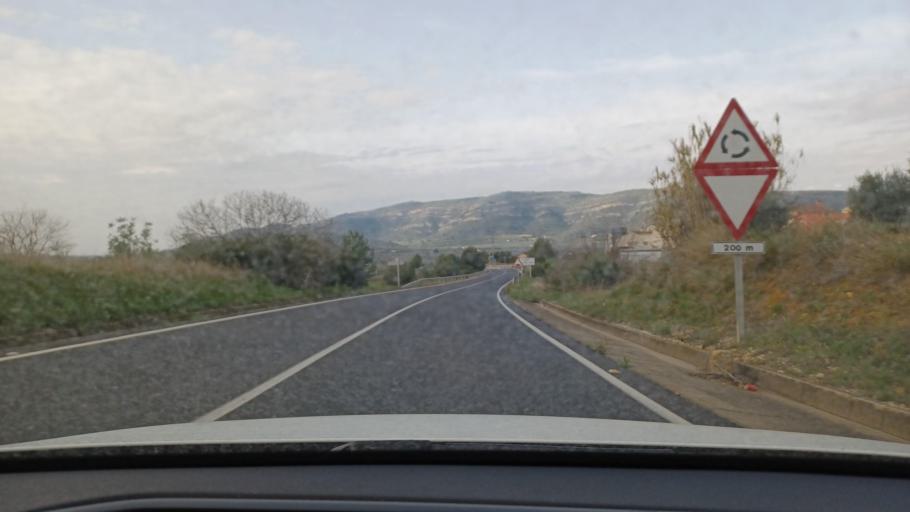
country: ES
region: Catalonia
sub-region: Provincia de Tarragona
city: Masdenverge
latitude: 40.6708
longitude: 0.5237
